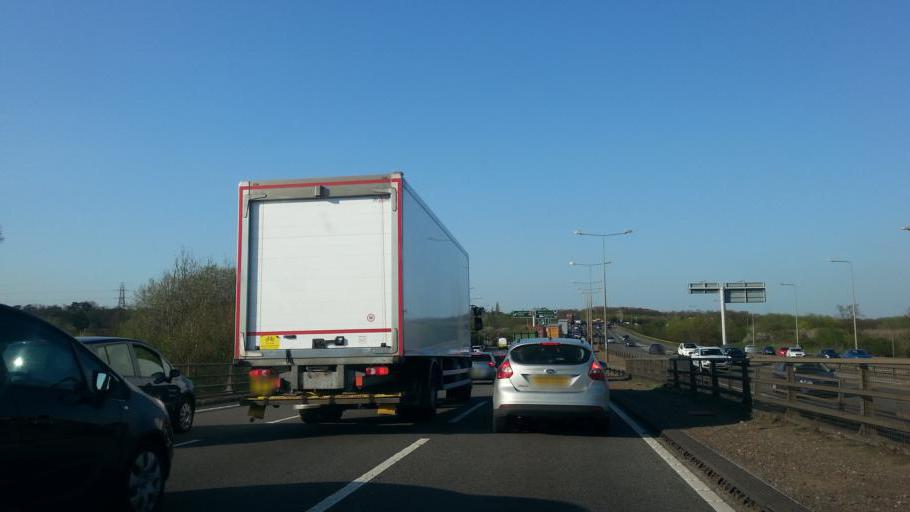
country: GB
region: England
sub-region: Northamptonshire
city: Hardingstone
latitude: 52.2271
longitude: -0.8715
